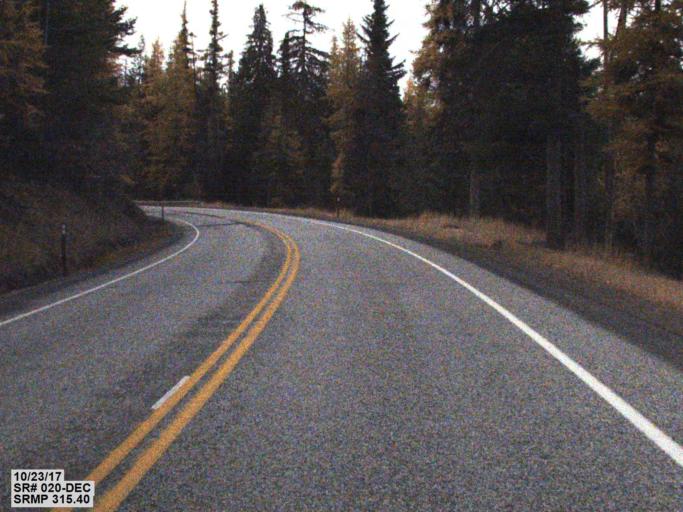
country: US
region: Washington
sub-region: Ferry County
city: Republic
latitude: 48.6068
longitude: -118.5377
